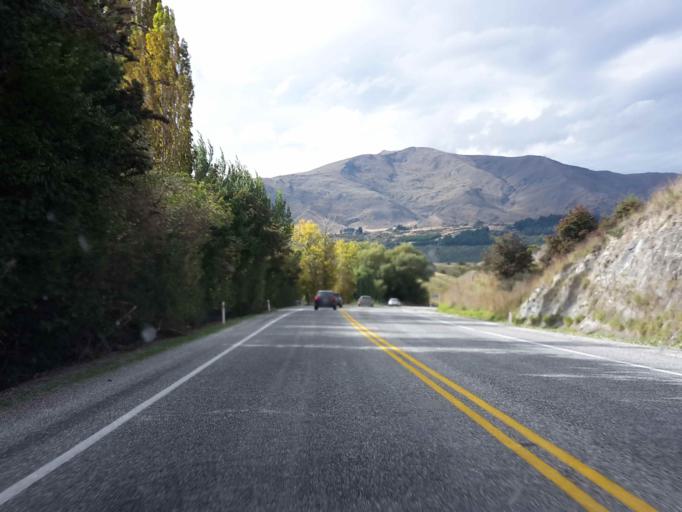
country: NZ
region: Otago
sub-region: Queenstown-Lakes District
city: Arrowtown
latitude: -44.9799
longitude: 168.8251
